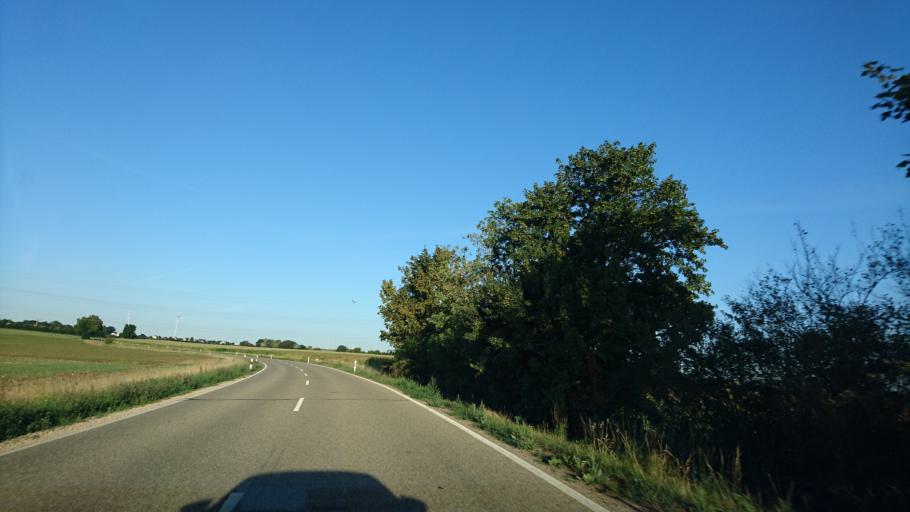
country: DE
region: Bavaria
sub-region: Regierungsbezirk Mittelfranken
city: Nennslingen
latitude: 49.0411
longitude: 11.1152
